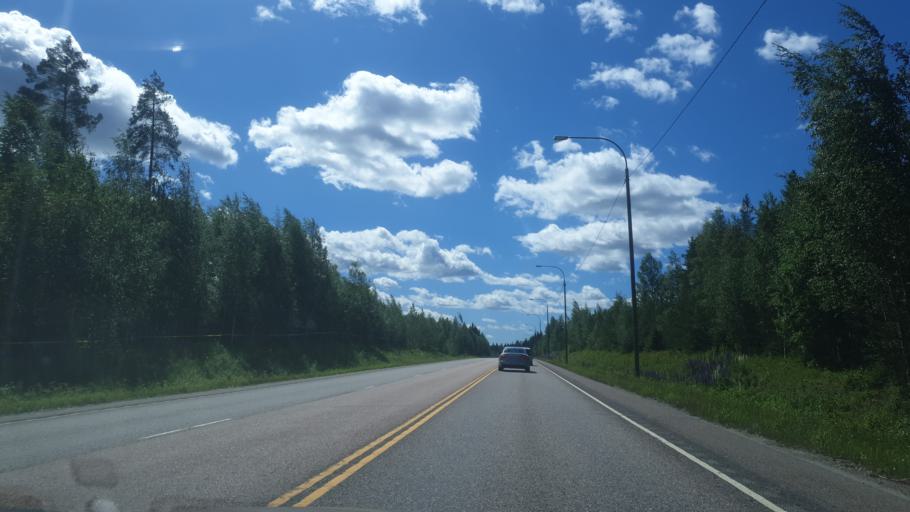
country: FI
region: Northern Savo
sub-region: Varkaus
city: Varkaus
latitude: 62.3928
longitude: 27.8160
